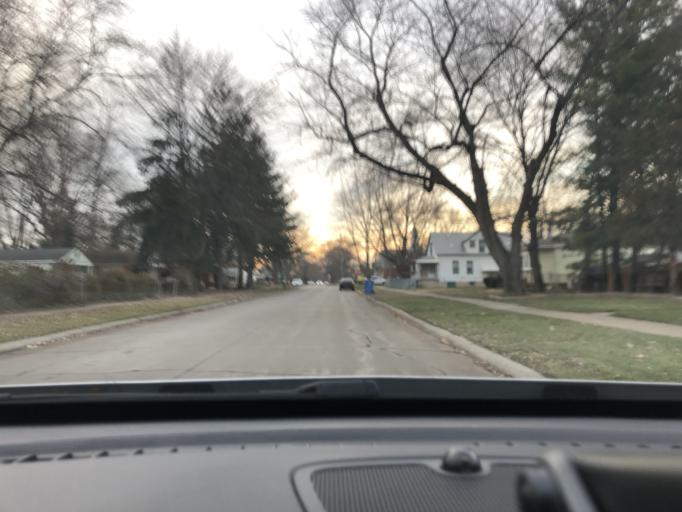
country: US
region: Michigan
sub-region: Wayne County
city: Allen Park
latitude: 42.2736
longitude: -83.2300
